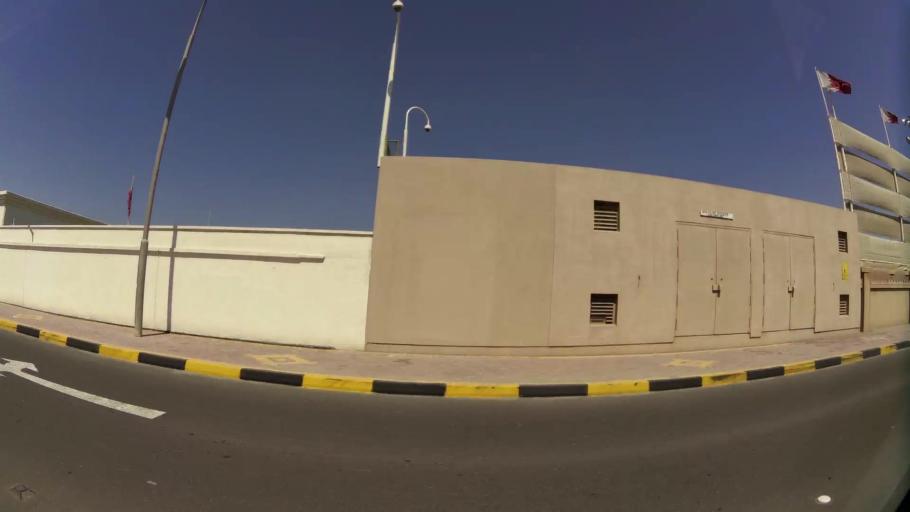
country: BH
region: Manama
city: Manama
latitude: 26.2206
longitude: 50.5924
